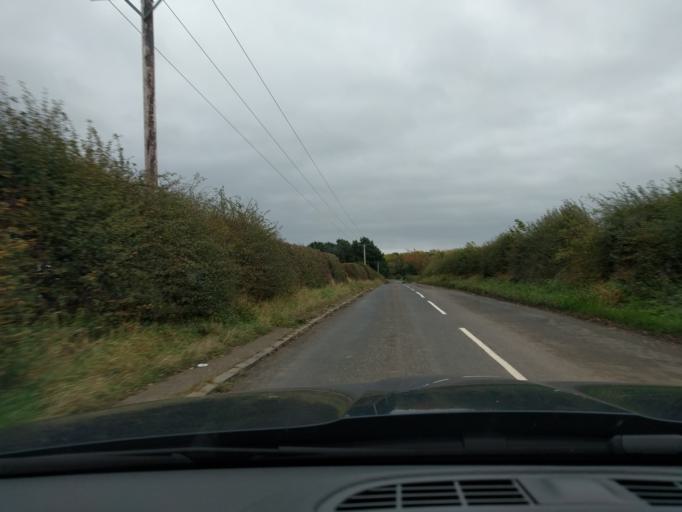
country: GB
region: Scotland
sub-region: The Scottish Borders
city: Allanton
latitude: 55.7167
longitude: -2.1519
